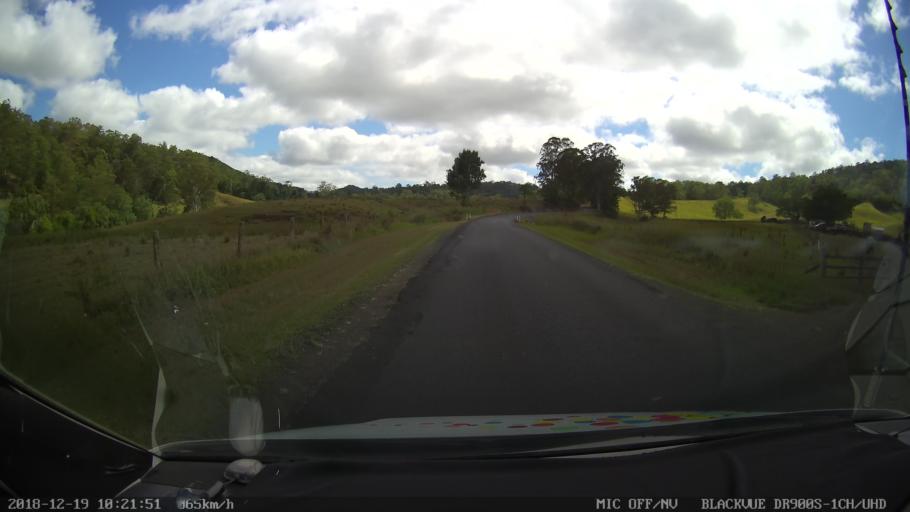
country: AU
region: New South Wales
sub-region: Kyogle
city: Kyogle
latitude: -28.5956
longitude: 153.0629
